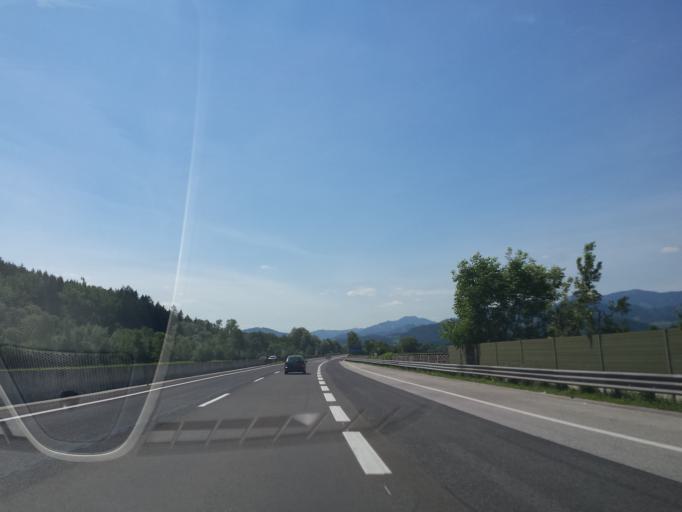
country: AT
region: Styria
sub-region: Politischer Bezirk Bruck-Muerzzuschlag
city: Sankt Marein im Muerztal
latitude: 47.4662
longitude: 15.3717
